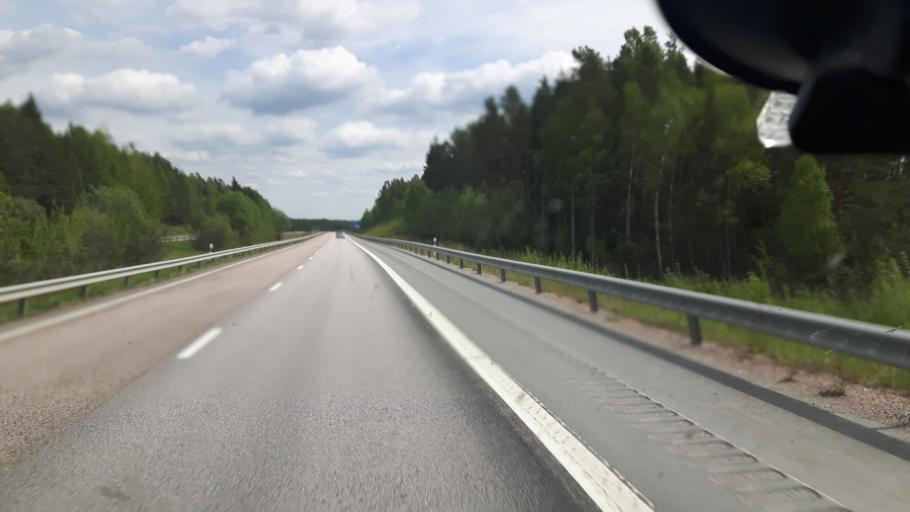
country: SE
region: Uppsala
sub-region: Alvkarleby Kommun
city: AElvkarleby
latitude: 60.4737
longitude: 17.3836
